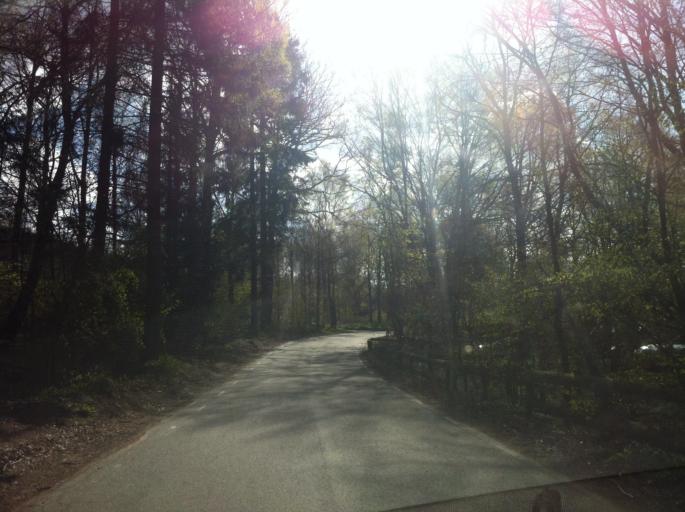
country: SE
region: Skane
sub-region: Hoors Kommun
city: Hoeoer
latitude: 55.9145
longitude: 13.4811
